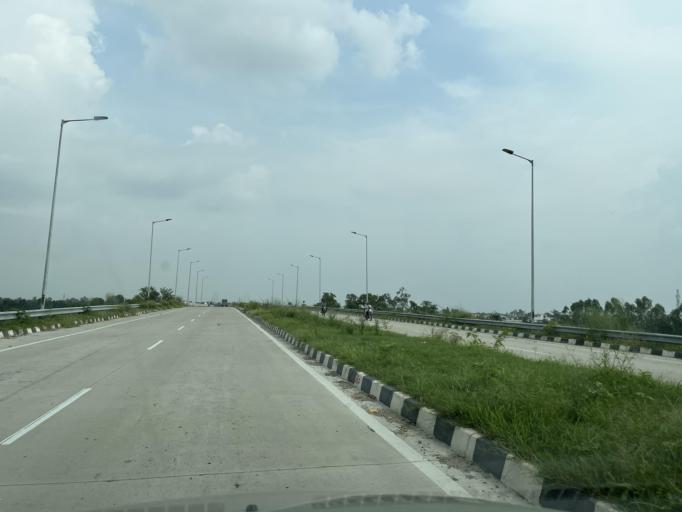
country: IN
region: Uttarakhand
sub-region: Udham Singh Nagar
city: Kashipur
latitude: 29.1747
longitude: 78.9443
